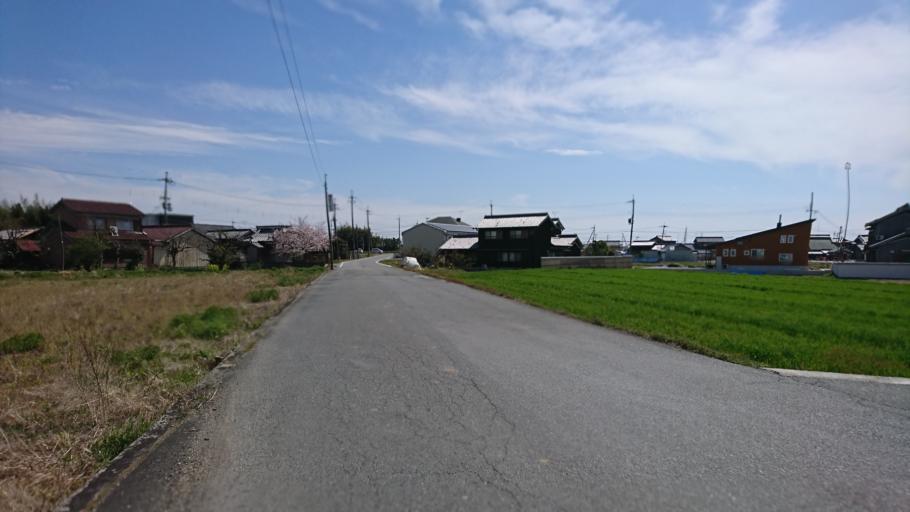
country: JP
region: Hyogo
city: Miki
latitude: 34.7549
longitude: 134.9350
